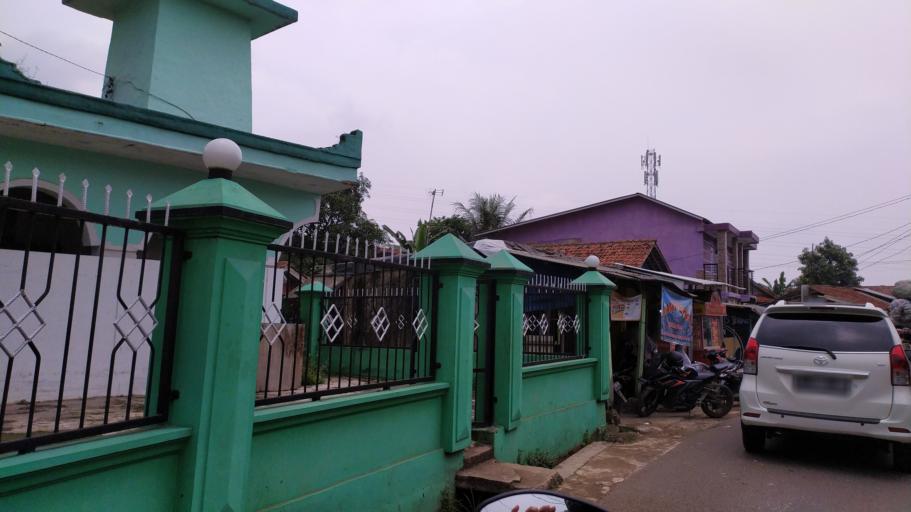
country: ID
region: West Java
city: Ciampea
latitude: -6.5916
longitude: 106.7038
